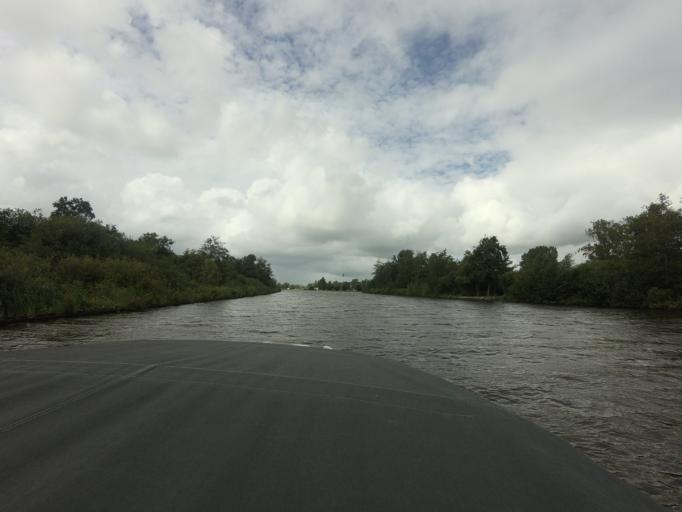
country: NL
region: Friesland
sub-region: Gemeente Tytsjerksteradiel
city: Garyp
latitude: 53.1221
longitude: 5.9428
